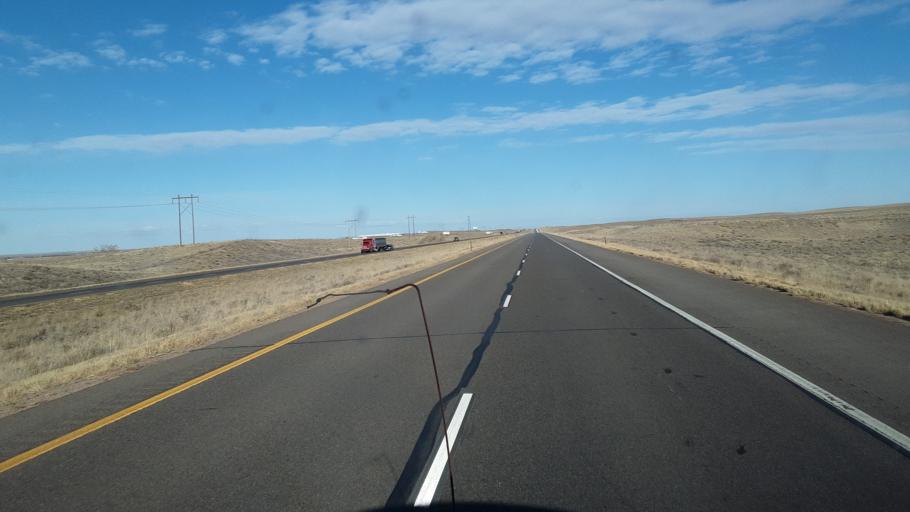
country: US
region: Colorado
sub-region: Morgan County
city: Brush
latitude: 40.3211
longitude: -103.4933
